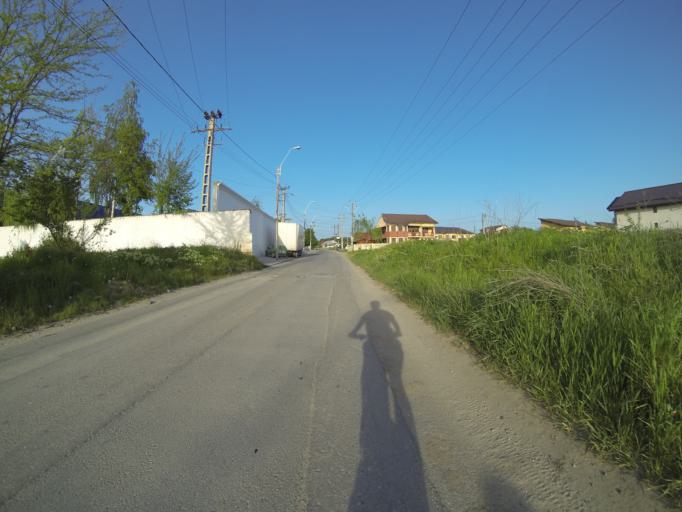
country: RO
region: Dolj
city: Craiova
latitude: 44.3222
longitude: 23.8450
